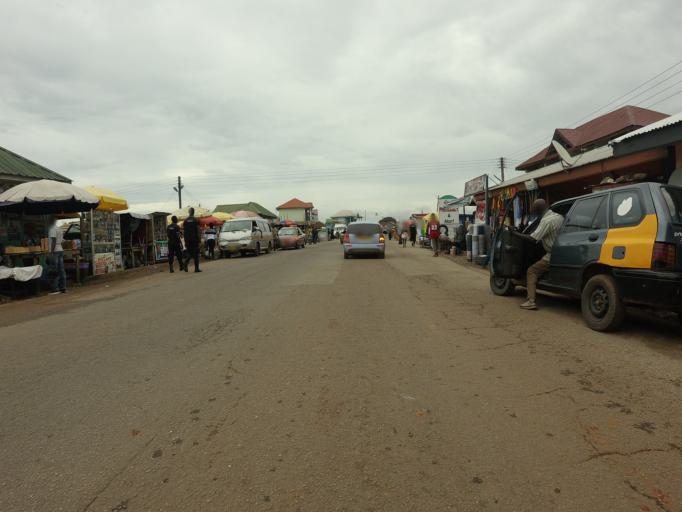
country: GH
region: Eastern
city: Begoro
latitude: 6.3808
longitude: -0.5492
